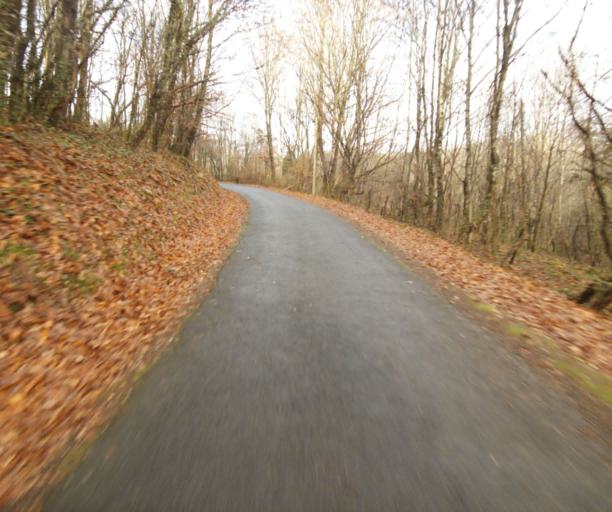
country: FR
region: Limousin
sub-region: Departement de la Correze
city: Saint-Mexant
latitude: 45.2570
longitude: 1.6419
